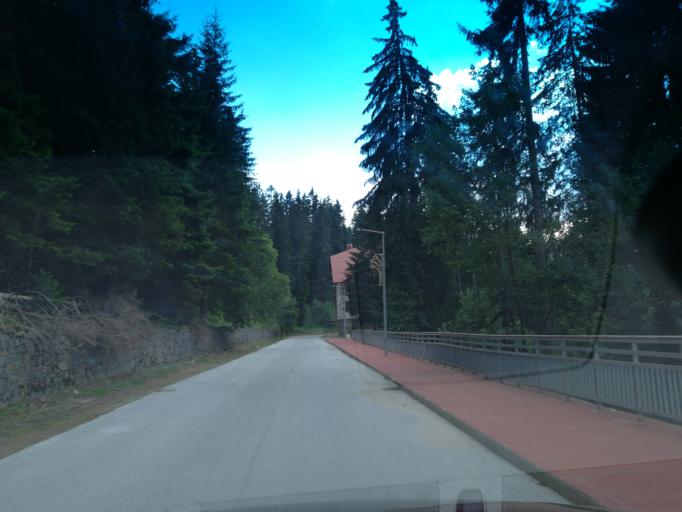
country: BG
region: Smolyan
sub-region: Obshtina Smolyan
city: Smolyan
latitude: 41.6565
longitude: 24.6943
